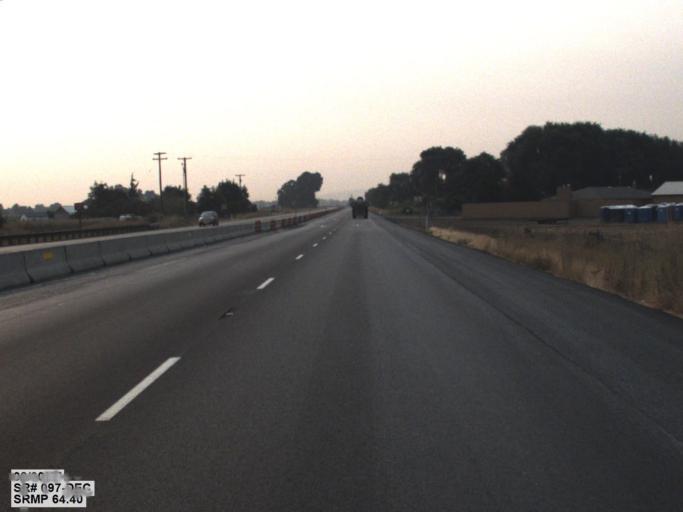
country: US
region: Washington
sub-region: Yakima County
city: Toppenish
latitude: 46.3968
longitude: -120.3687
